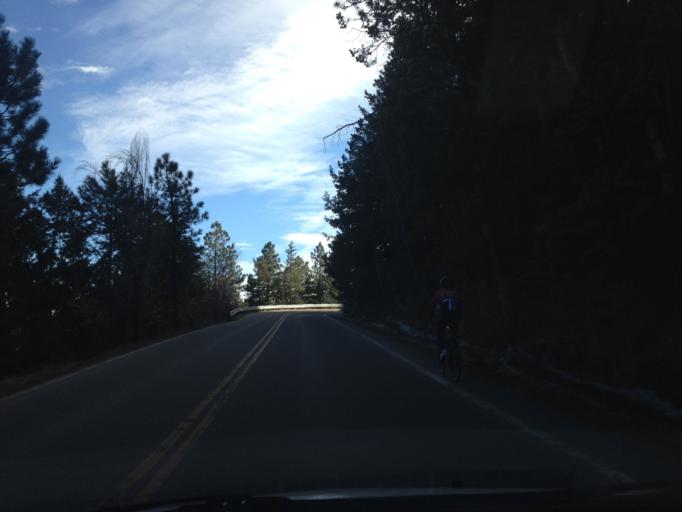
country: US
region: Colorado
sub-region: Boulder County
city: Boulder
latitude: 40.0037
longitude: -105.2951
